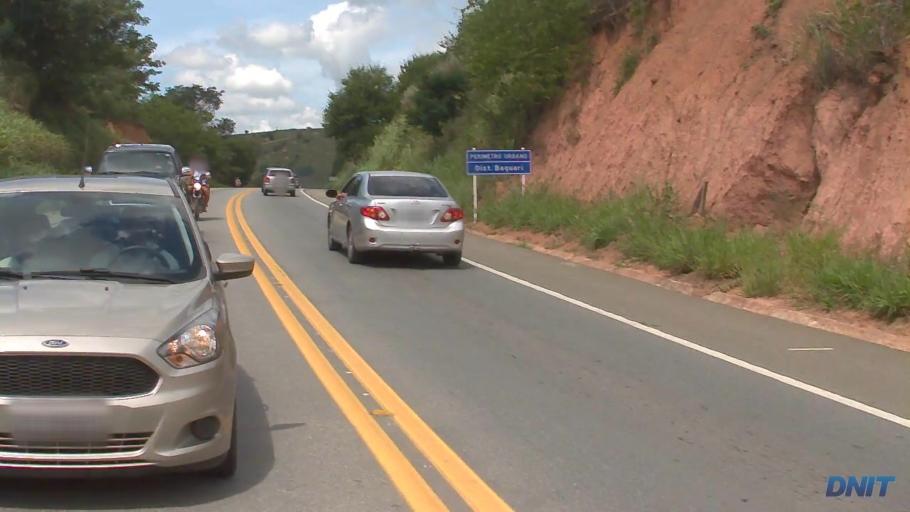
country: BR
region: Minas Gerais
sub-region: Governador Valadares
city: Governador Valadares
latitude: -18.9657
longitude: -42.0817
